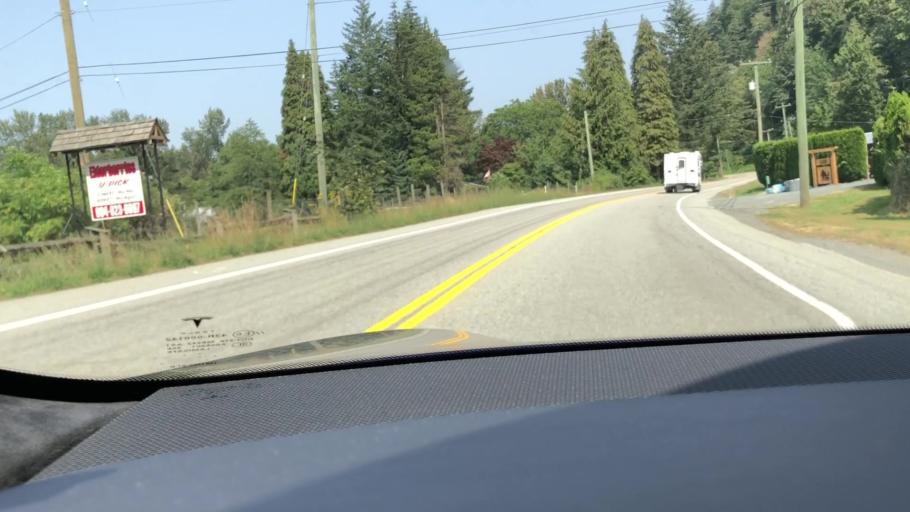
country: CA
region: British Columbia
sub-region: Fraser Valley Regional District
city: Chilliwack
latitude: 49.0925
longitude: -121.9929
